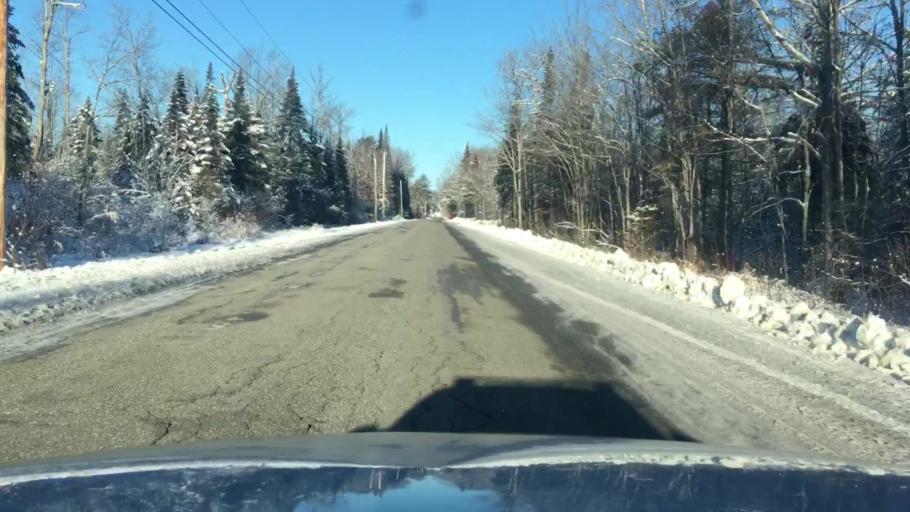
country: US
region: Maine
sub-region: Kennebec County
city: Belgrade
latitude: 44.4087
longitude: -69.8639
